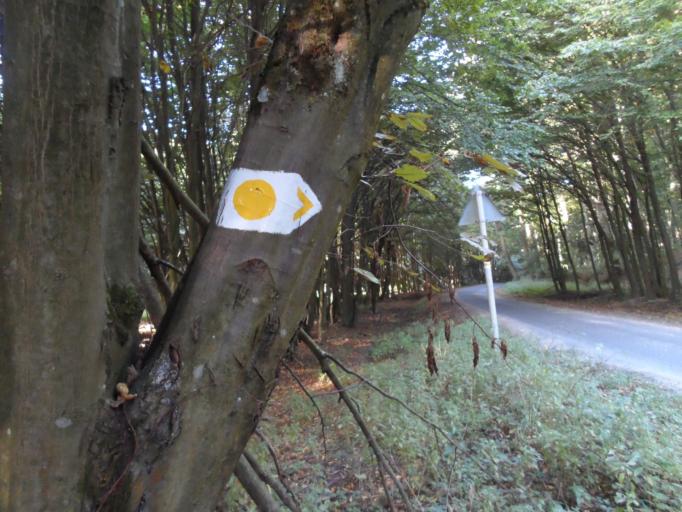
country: HU
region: Veszprem
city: Zirc
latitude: 47.2729
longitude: 17.7650
